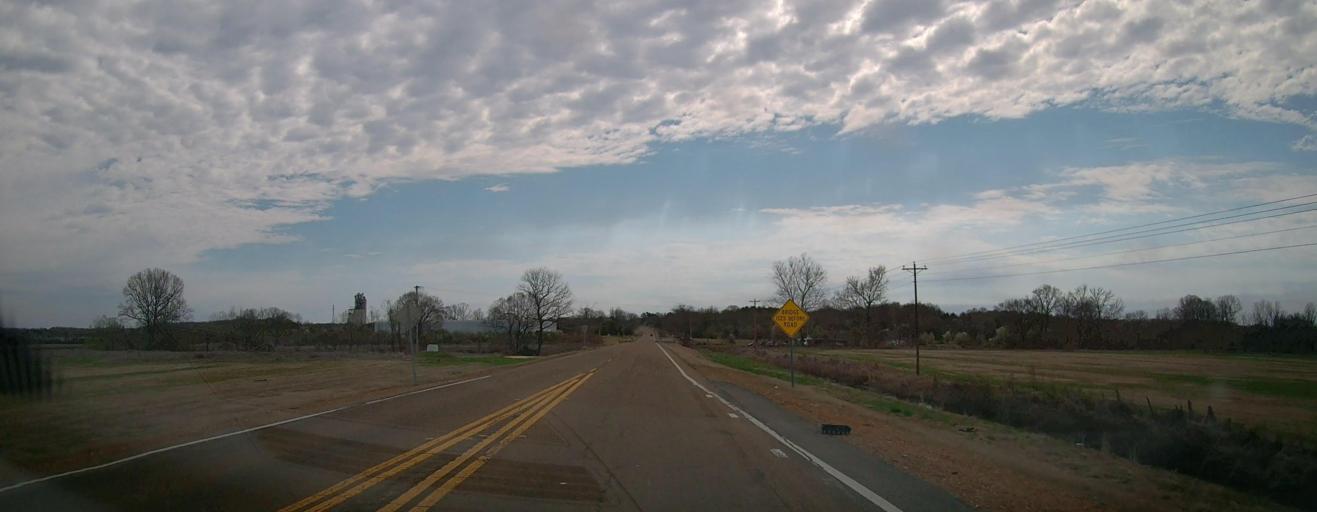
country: US
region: Mississippi
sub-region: Marshall County
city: Byhalia
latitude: 34.8665
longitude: -89.6651
